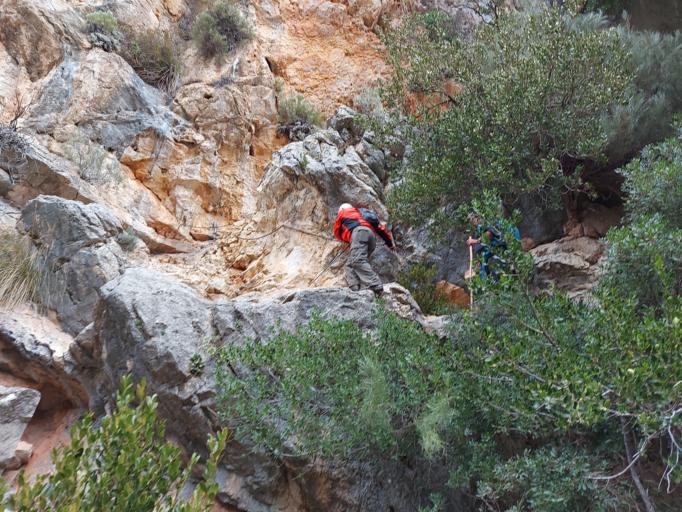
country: ES
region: Balearic Islands
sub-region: Illes Balears
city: Fornalutx
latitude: 39.7746
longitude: 2.8043
